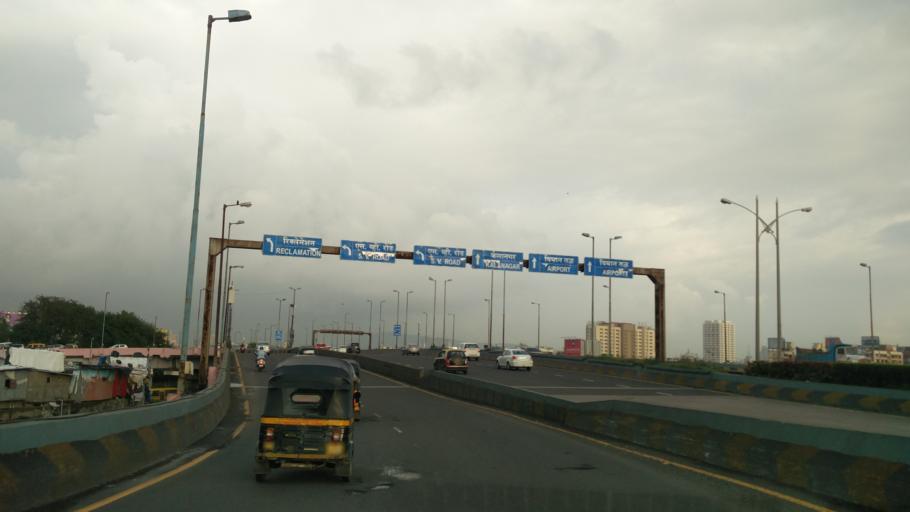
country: IN
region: Maharashtra
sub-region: Mumbai Suburban
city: Mumbai
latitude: 19.0502
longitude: 72.8354
